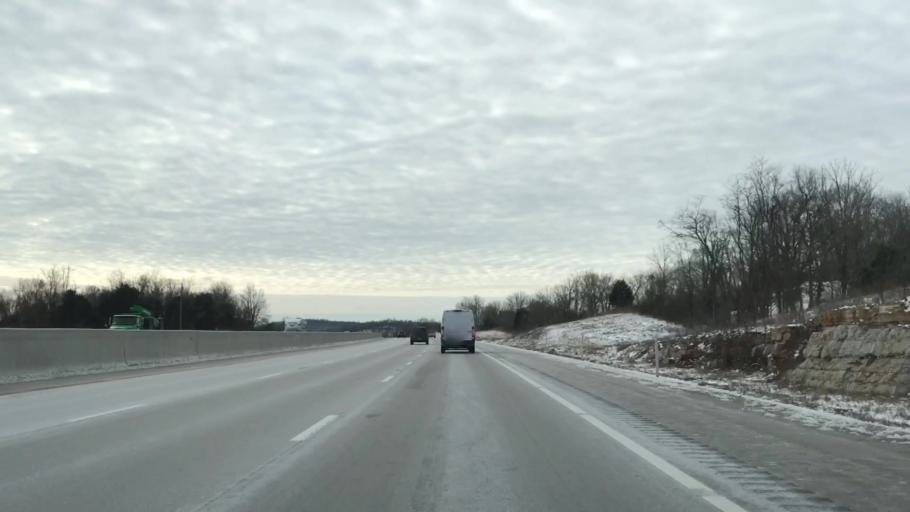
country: US
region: Kentucky
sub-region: Hart County
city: Munfordville
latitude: 37.2697
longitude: -85.9183
